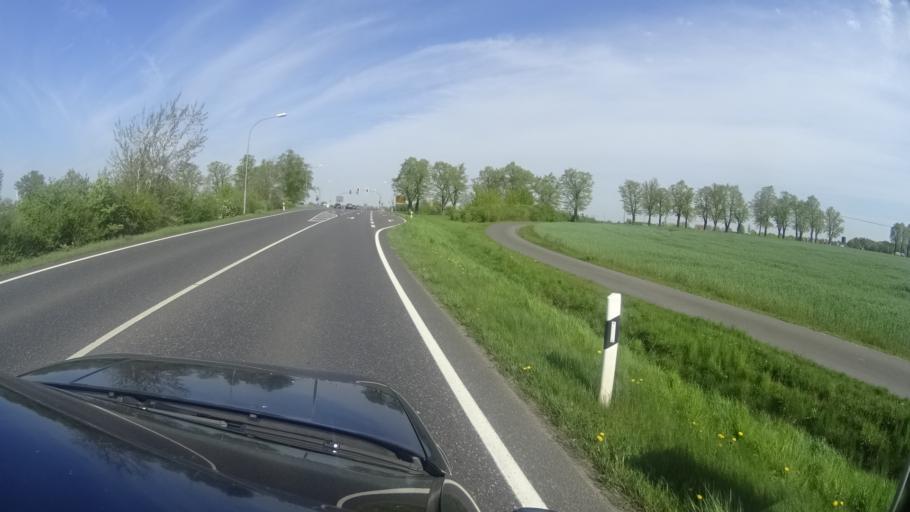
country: DE
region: Brandenburg
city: Nauen
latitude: 52.5991
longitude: 12.8525
